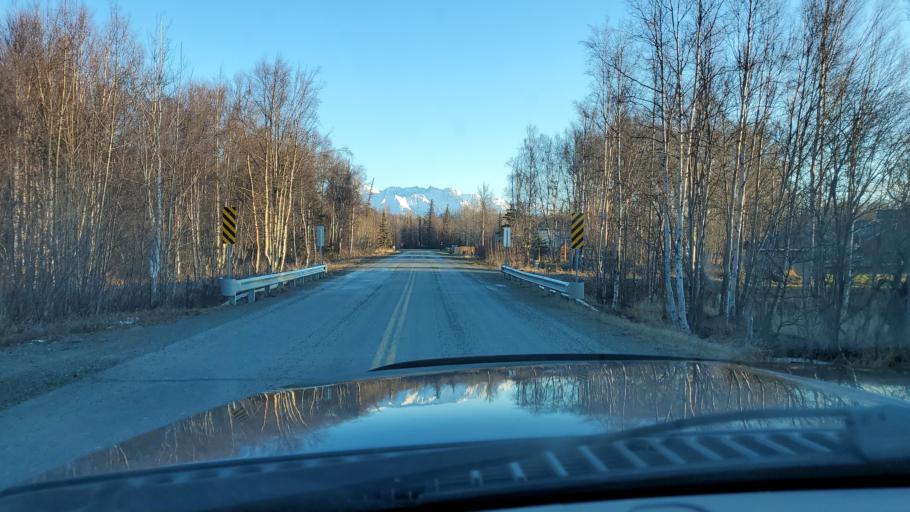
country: US
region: Alaska
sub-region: Matanuska-Susitna Borough
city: Gateway
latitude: 61.5885
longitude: -149.2521
